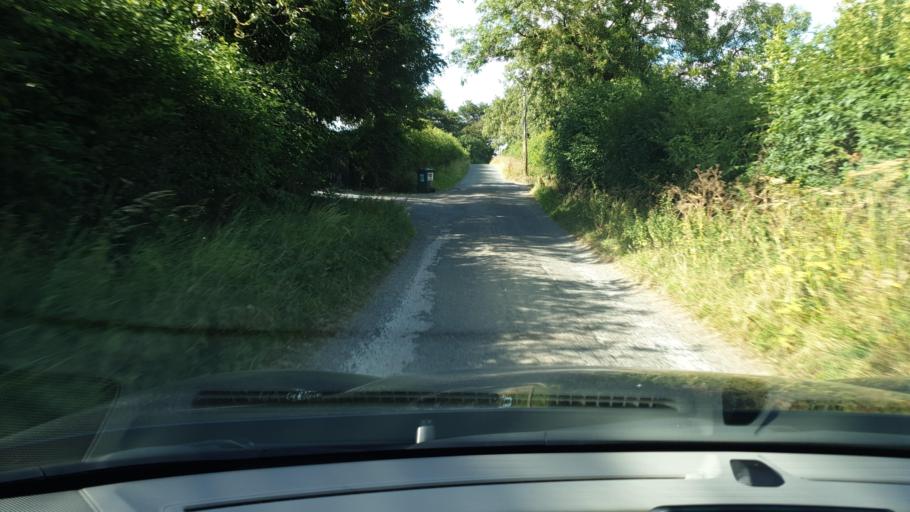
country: IE
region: Leinster
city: Hartstown
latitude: 53.4502
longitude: -6.4271
